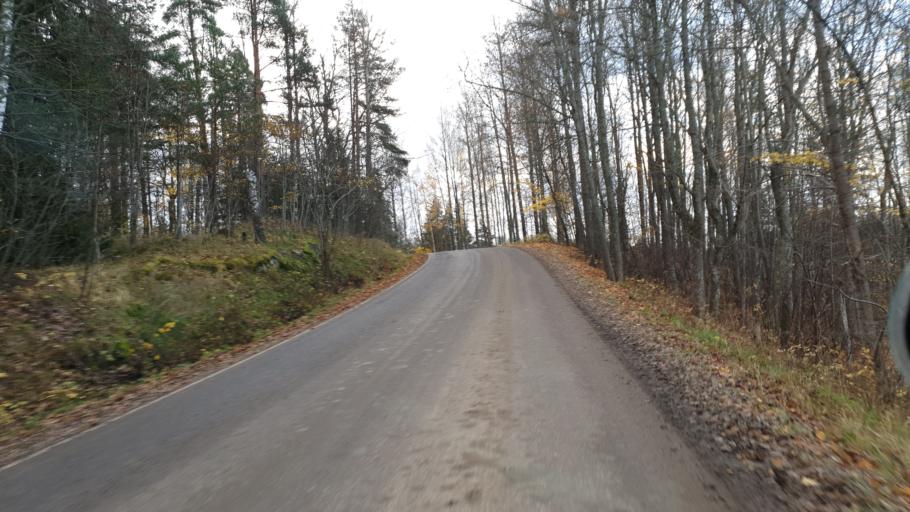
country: FI
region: Uusimaa
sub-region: Helsinki
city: Siuntio
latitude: 60.1006
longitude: 24.2987
